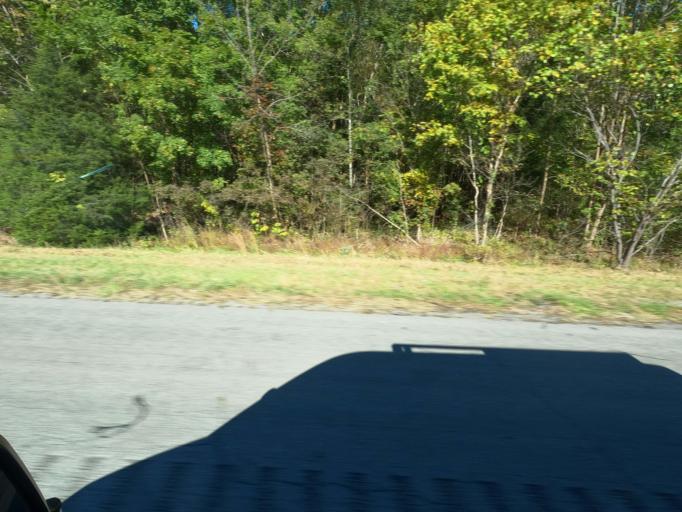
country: US
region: Tennessee
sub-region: Dickson County
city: White Bluff
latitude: 36.0242
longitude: -87.2241
